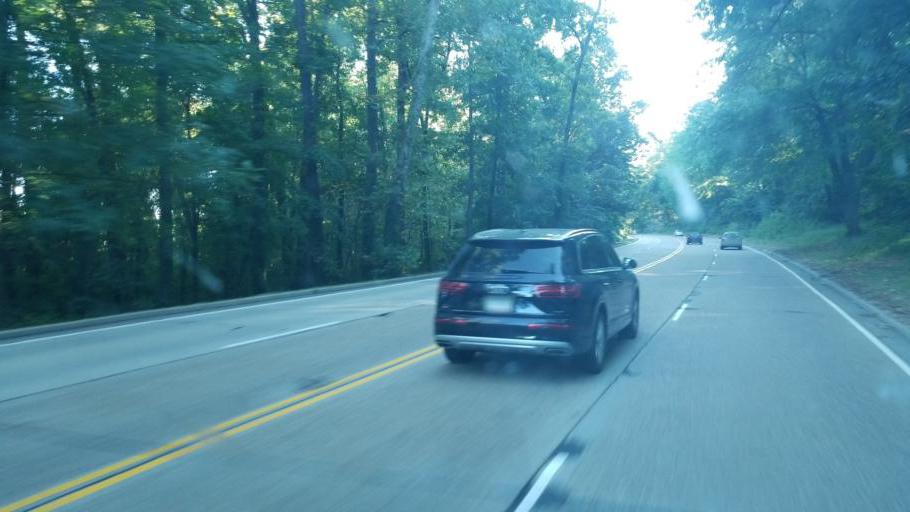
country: US
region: Virginia
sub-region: Fairfax County
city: Fort Hunt
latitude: 38.7551
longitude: -77.0497
